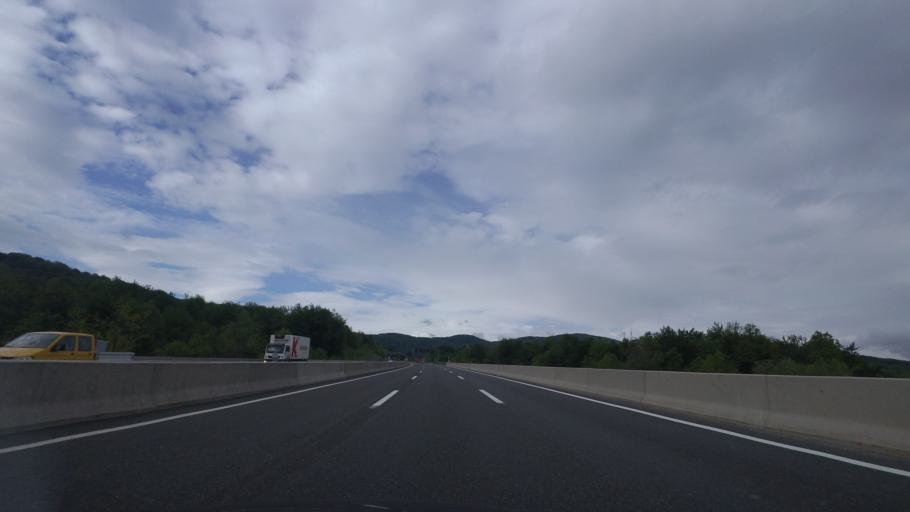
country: HR
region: Primorsko-Goranska
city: Vrbovsko
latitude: 45.3923
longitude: 15.1999
